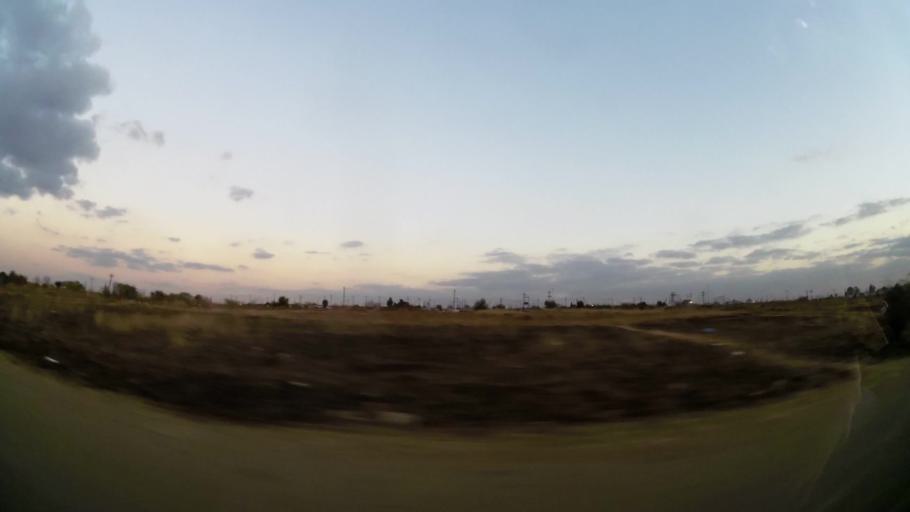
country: ZA
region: Gauteng
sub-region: West Rand District Municipality
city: Krugersdorp
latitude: -26.0729
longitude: 27.6565
